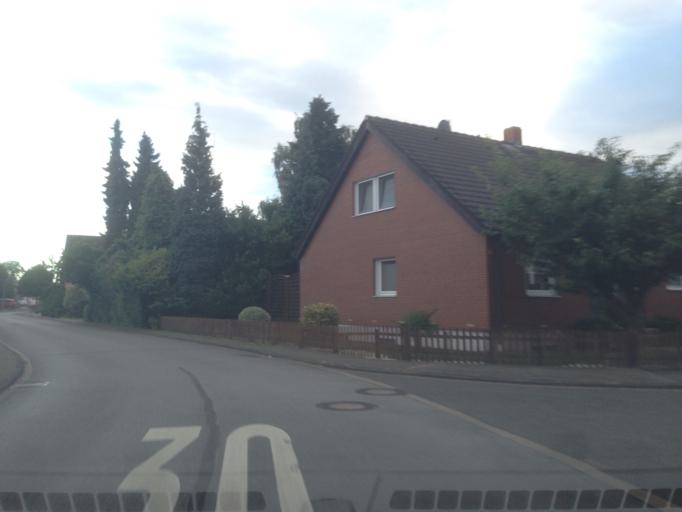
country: DE
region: North Rhine-Westphalia
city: Olfen
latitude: 51.7112
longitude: 7.3752
